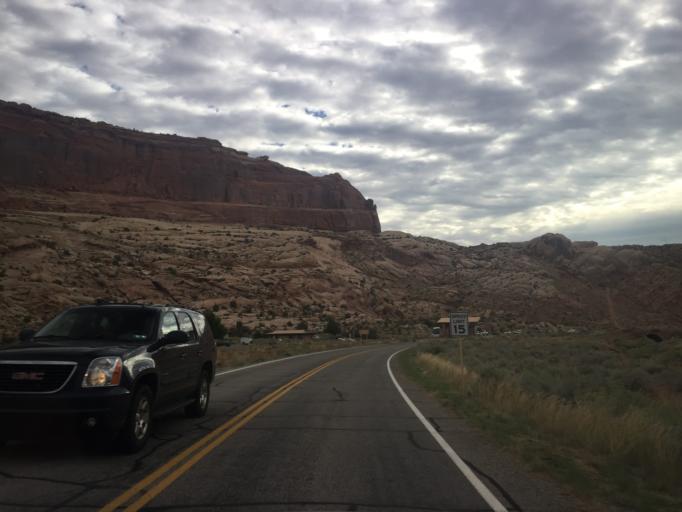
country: US
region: Utah
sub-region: Grand County
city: Moab
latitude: 38.6164
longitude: -109.6187
